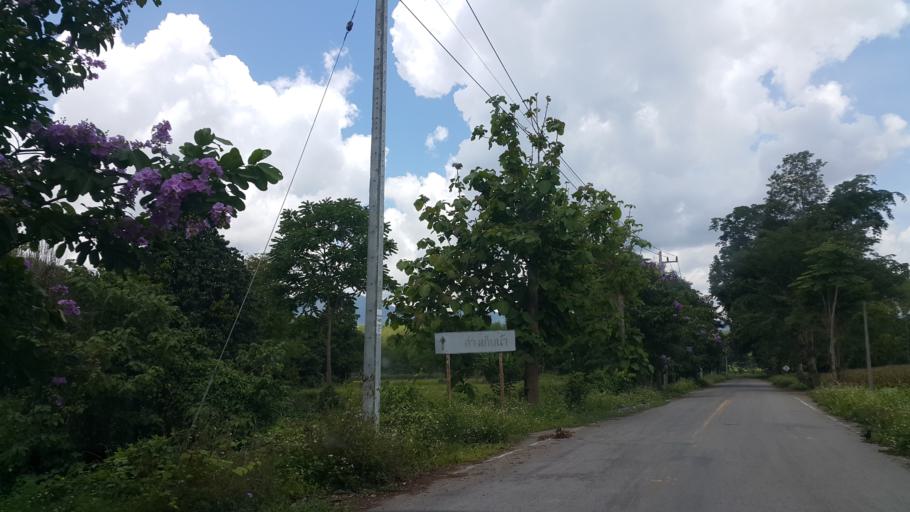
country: TH
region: Phayao
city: Phayao
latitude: 19.1859
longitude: 99.8036
